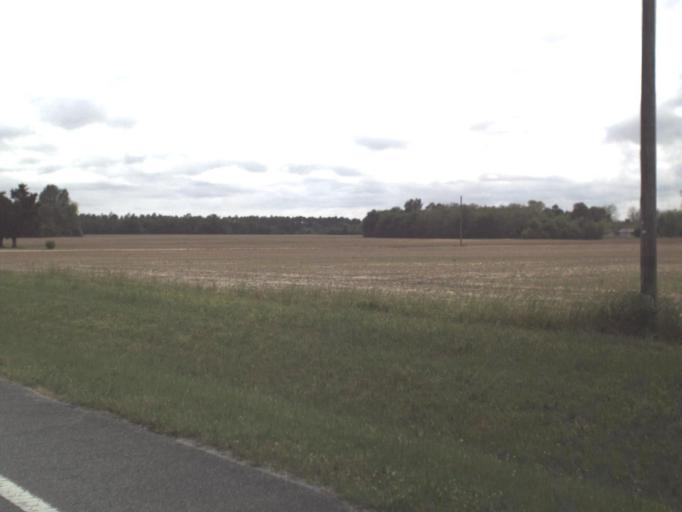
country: US
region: Florida
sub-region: Santa Rosa County
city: Point Baker
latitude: 30.7082
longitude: -87.0785
